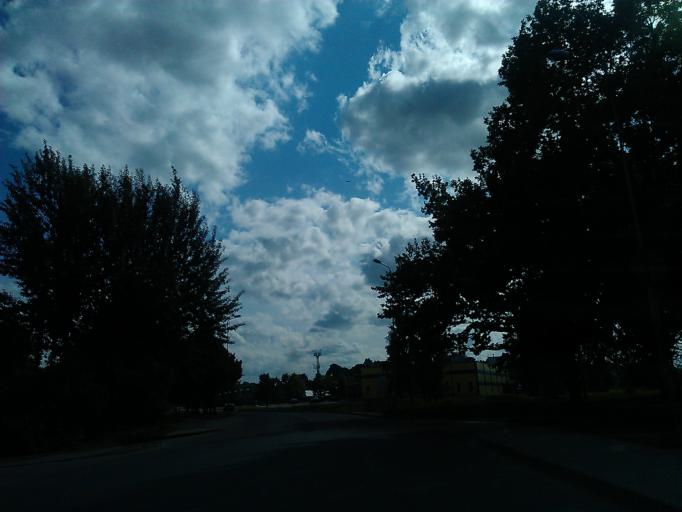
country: LV
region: Cesu Rajons
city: Cesis
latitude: 57.3146
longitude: 25.2877
